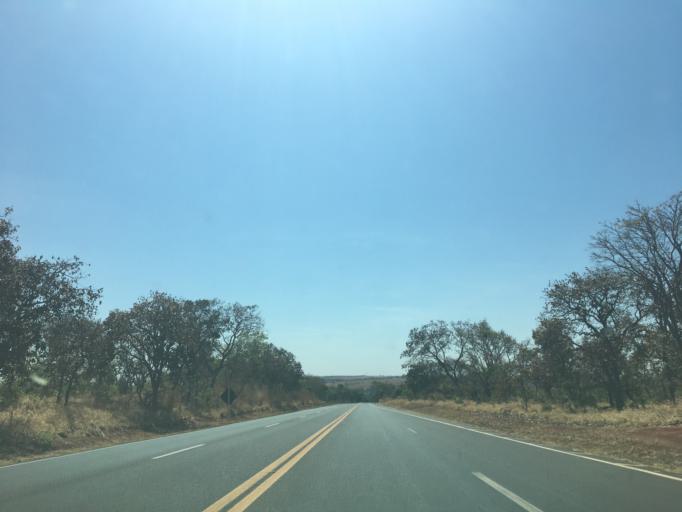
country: BR
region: Minas Gerais
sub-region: Monte Alegre De Minas
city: Monte Alegre de Minas
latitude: -18.8954
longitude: -49.0454
